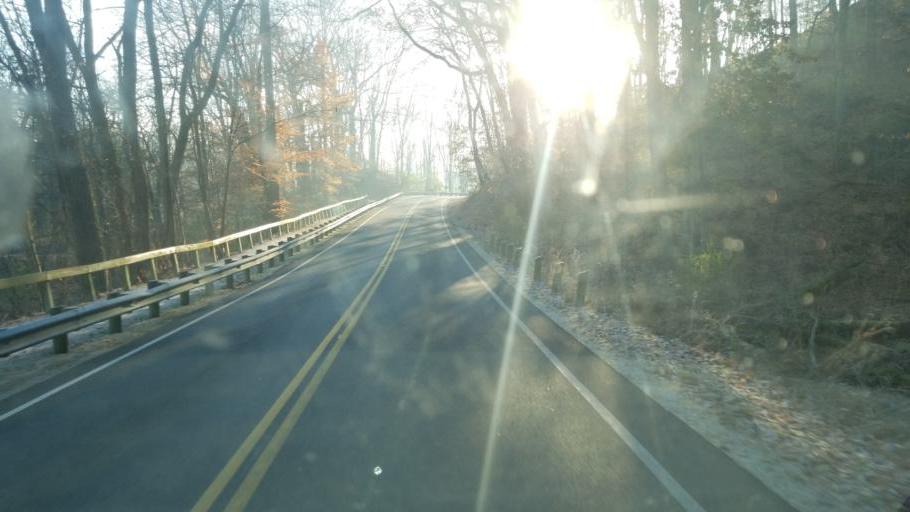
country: US
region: Ohio
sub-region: Summit County
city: Fairlawn
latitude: 41.1363
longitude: -81.5603
